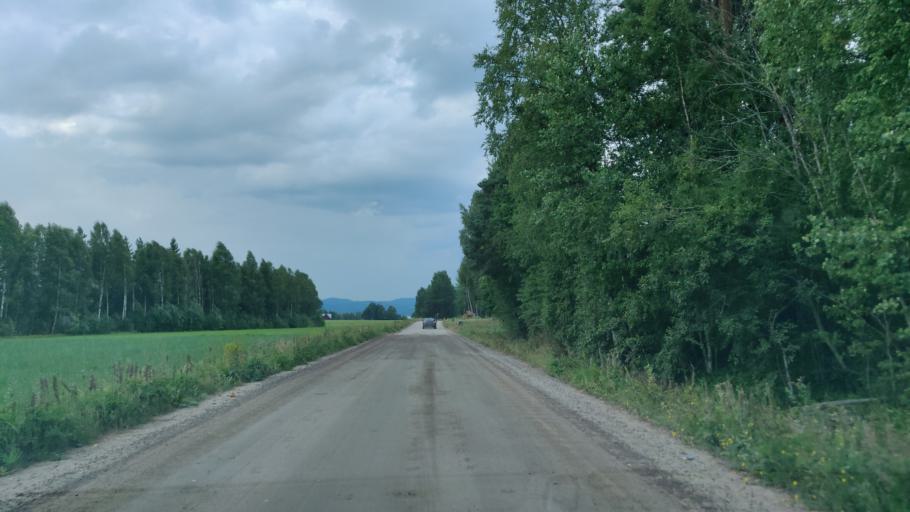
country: SE
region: Vaermland
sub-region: Munkfors Kommun
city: Munkfors
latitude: 59.9631
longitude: 13.4921
